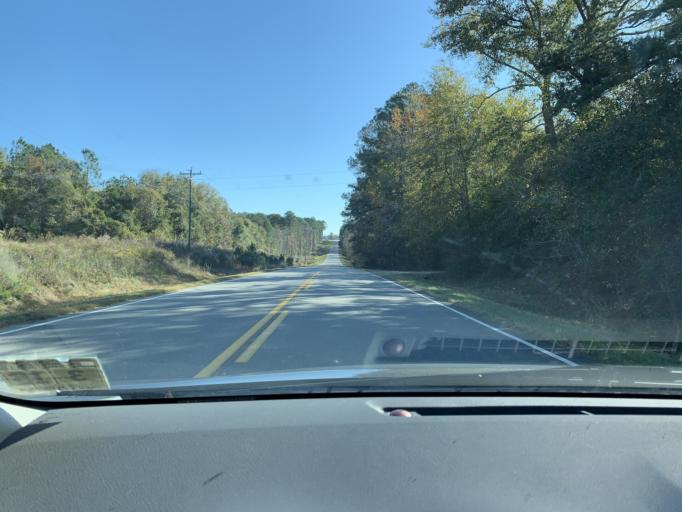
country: US
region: Georgia
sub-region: Coffee County
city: Broxton
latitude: 31.7688
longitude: -83.0245
